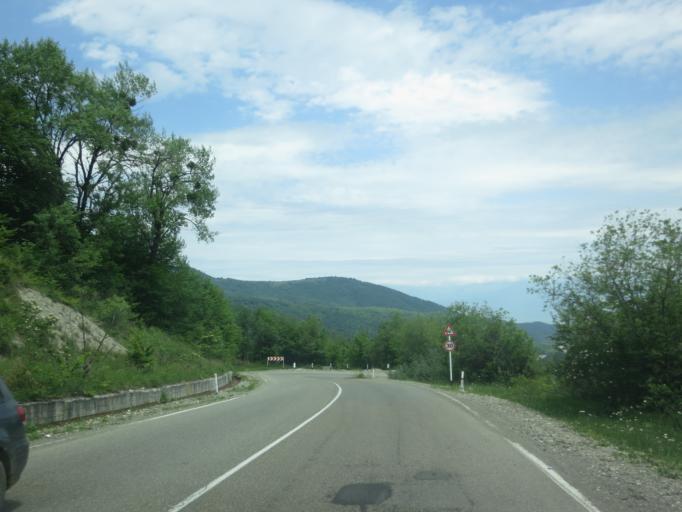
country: GE
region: Kakheti
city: Sagarejo
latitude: 41.8663
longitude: 45.3472
